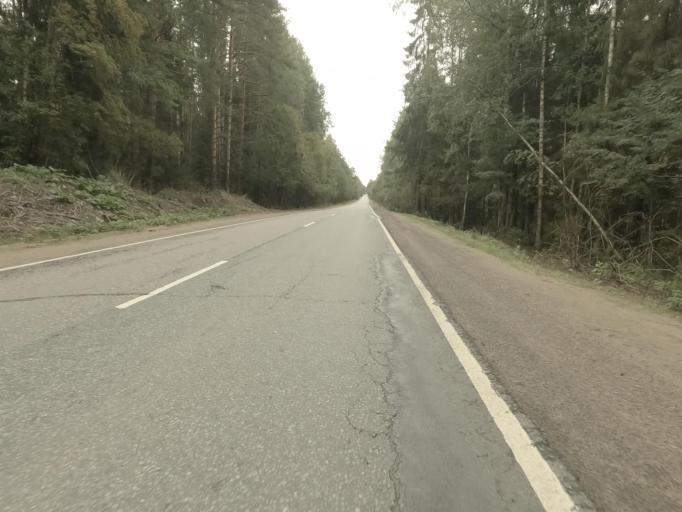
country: RU
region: Leningrad
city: Koltushi
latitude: 59.8987
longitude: 30.7614
